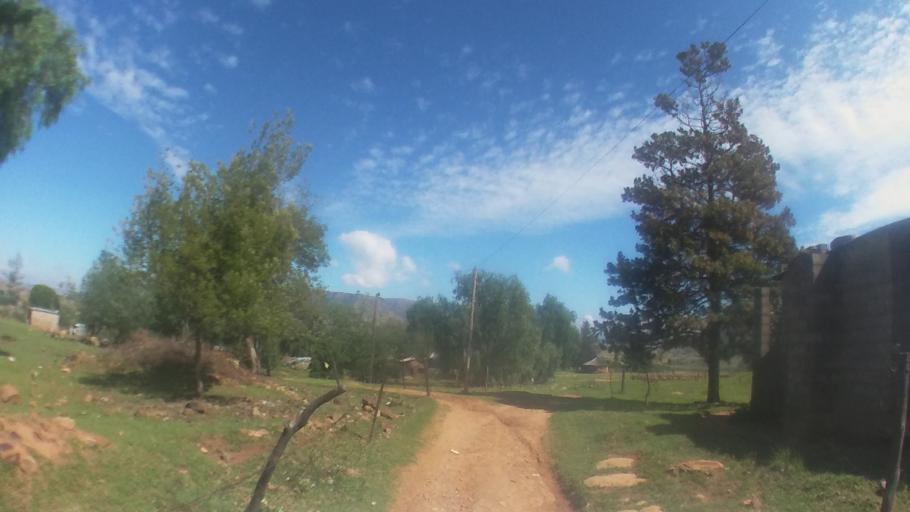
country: LS
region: Maseru
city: Nako
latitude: -29.6252
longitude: 27.5133
